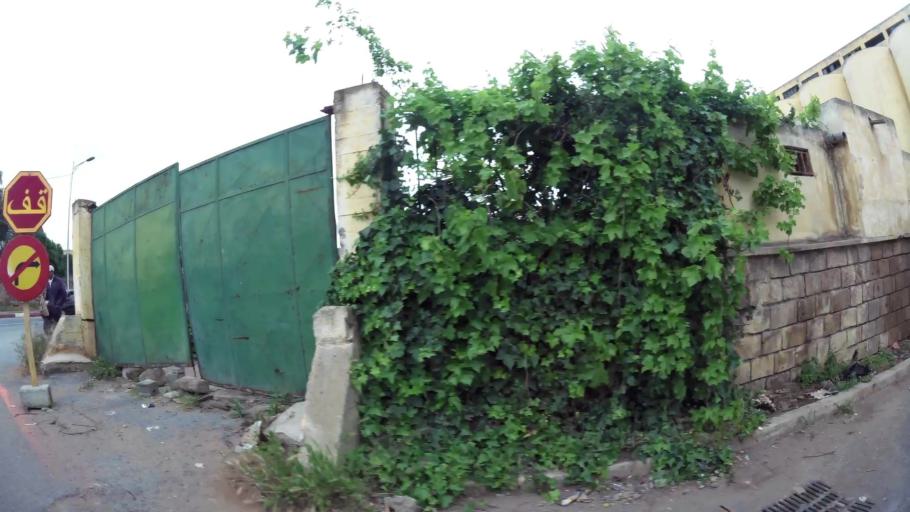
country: MA
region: Grand Casablanca
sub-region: Casablanca
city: Casablanca
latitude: 33.5475
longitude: -7.6400
